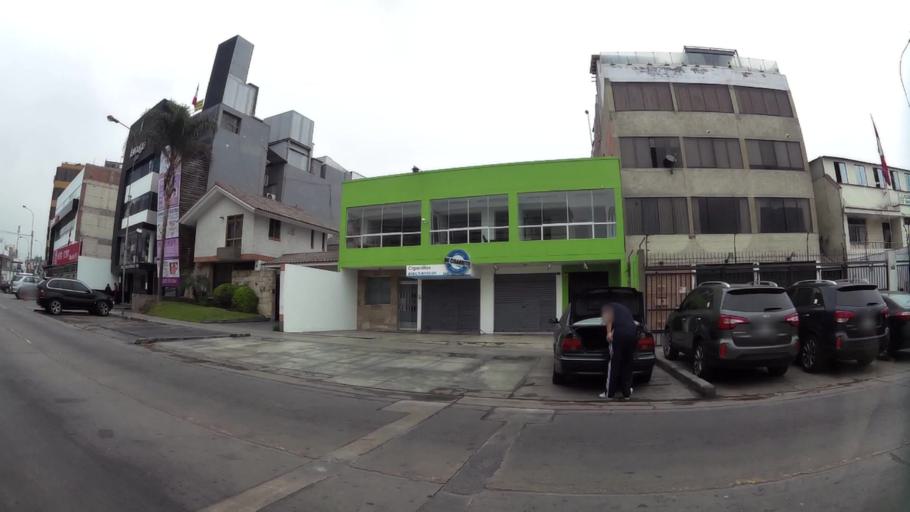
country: PE
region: Lima
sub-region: Lima
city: San Luis
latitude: -12.0915
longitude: -77.0053
